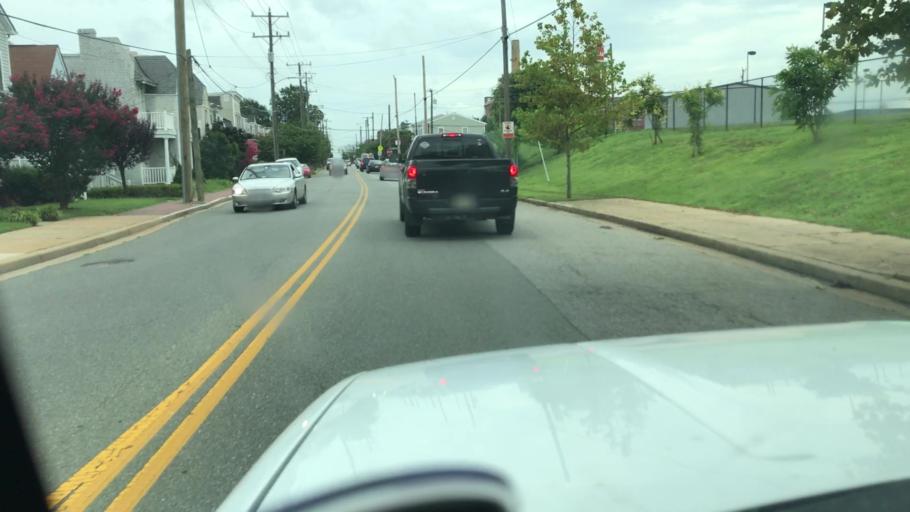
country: US
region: Virginia
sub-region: City of Richmond
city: Richmond
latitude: 37.5590
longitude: -77.4569
